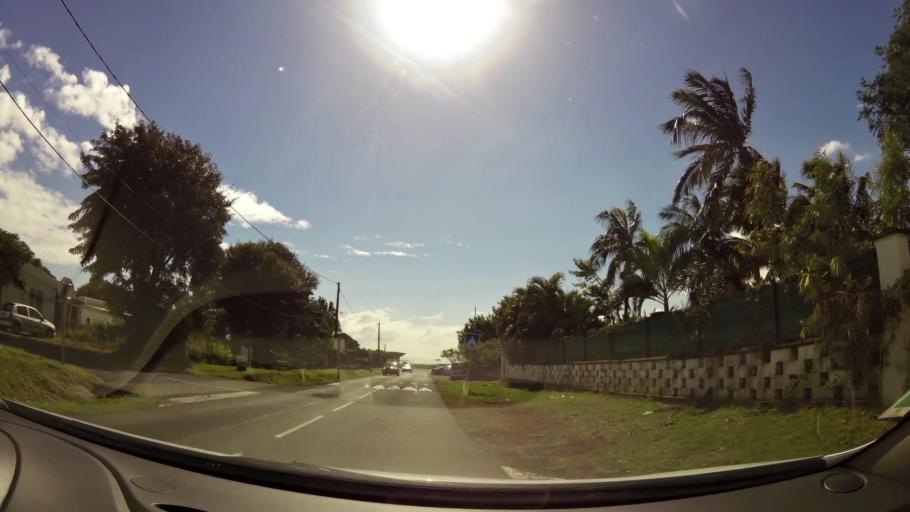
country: RE
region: Reunion
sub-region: Reunion
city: Sainte-Marie
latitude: -20.8921
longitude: 55.5095
